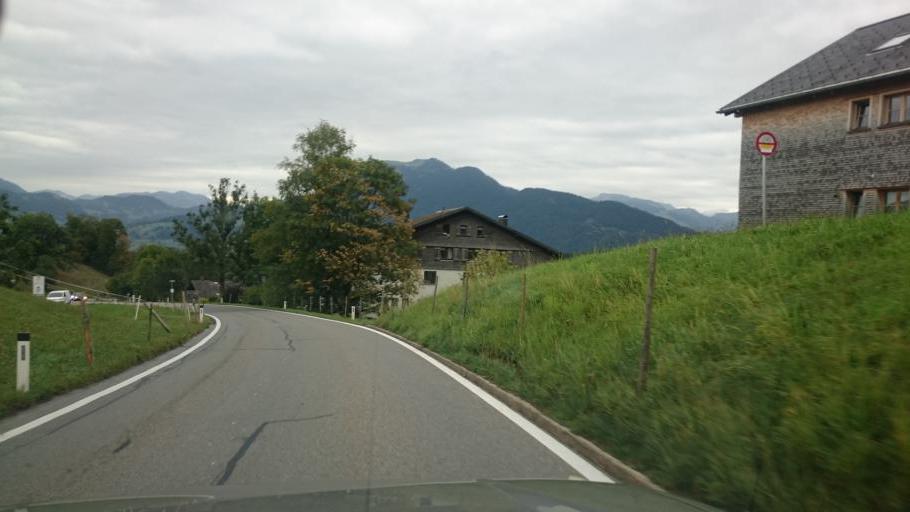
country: AT
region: Vorarlberg
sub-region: Politischer Bezirk Bregenz
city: Andelsbuch
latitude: 47.4143
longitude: 9.8453
